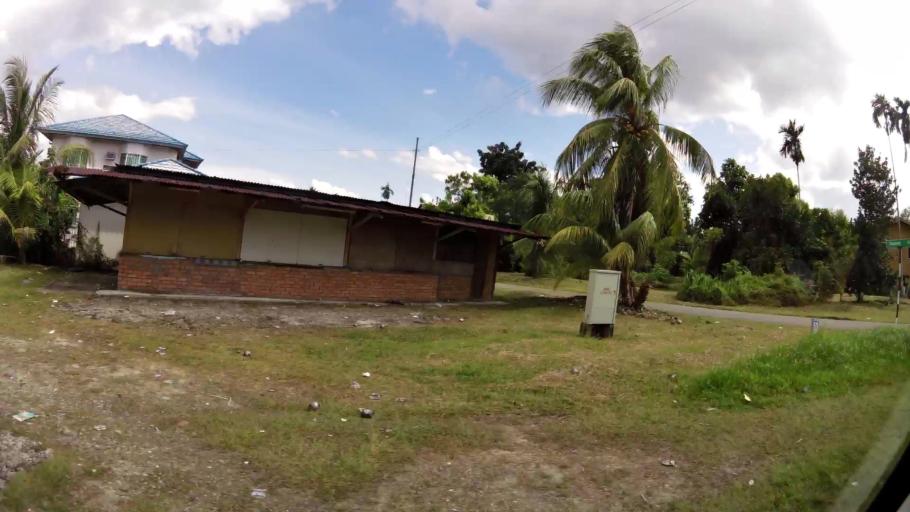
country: BN
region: Brunei and Muara
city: Bandar Seri Begawan
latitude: 4.9564
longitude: 114.9535
